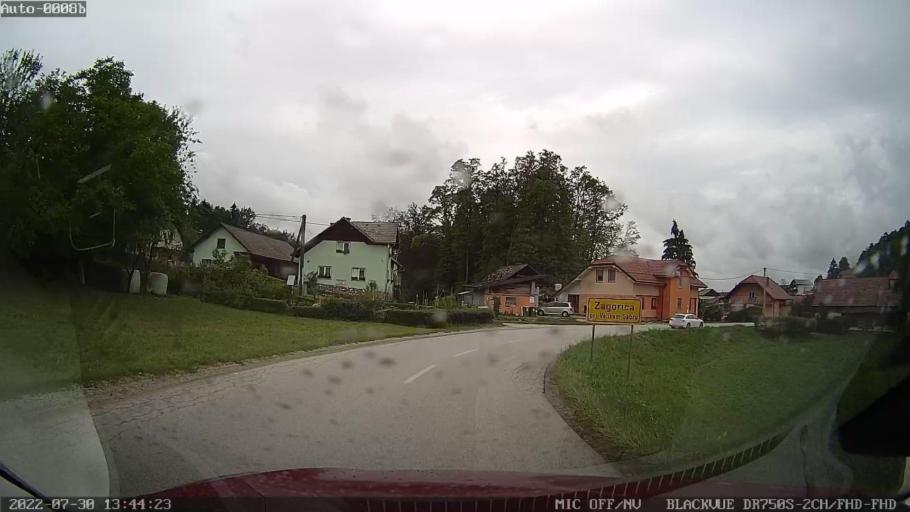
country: SI
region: Ivancna Gorica
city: Sentvid pri Sticni
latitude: 45.9172
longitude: 14.8915
